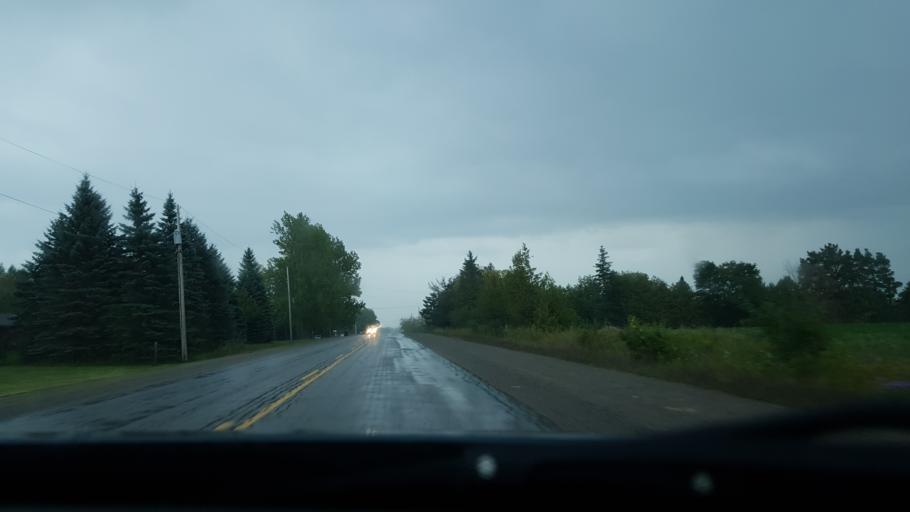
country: CA
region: Ontario
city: Omemee
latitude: 44.3866
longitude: -78.5537
